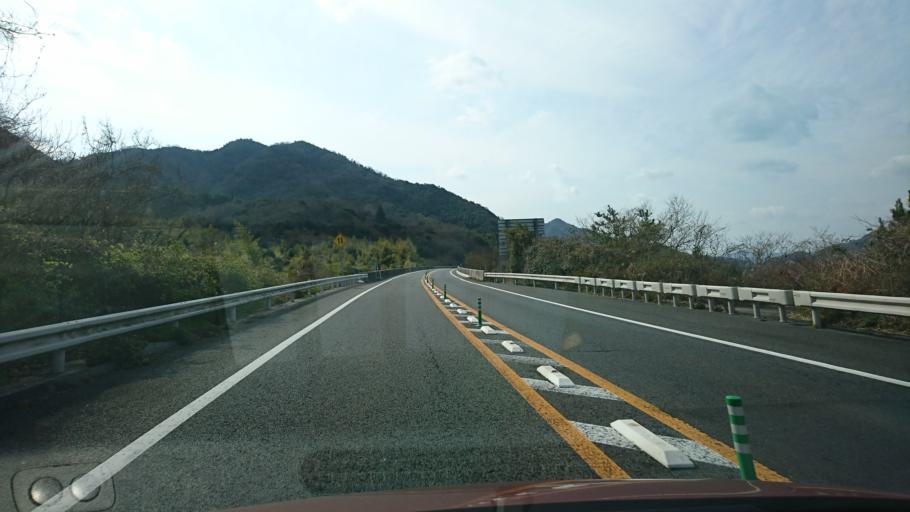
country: JP
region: Hiroshima
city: Innoshima
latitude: 34.1361
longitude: 133.0524
